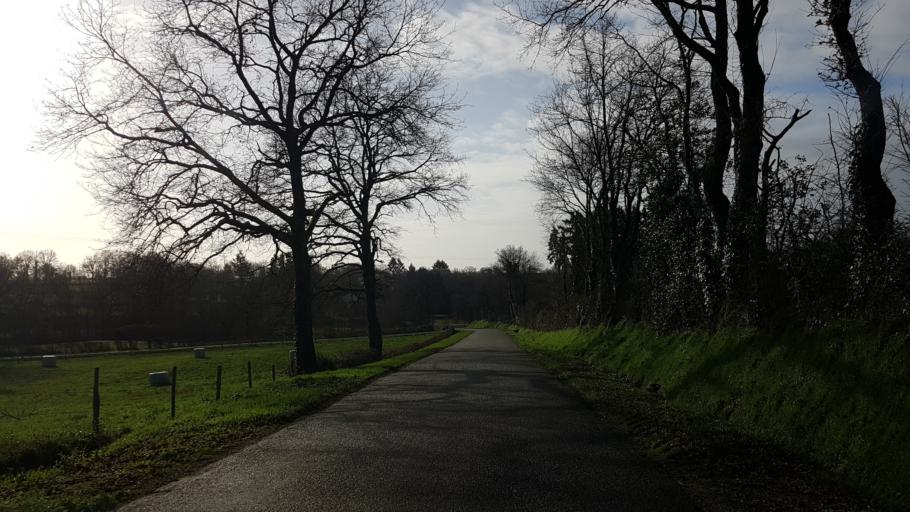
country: FR
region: Poitou-Charentes
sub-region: Departement de la Charente
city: Etagnac
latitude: 45.8916
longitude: 0.7749
